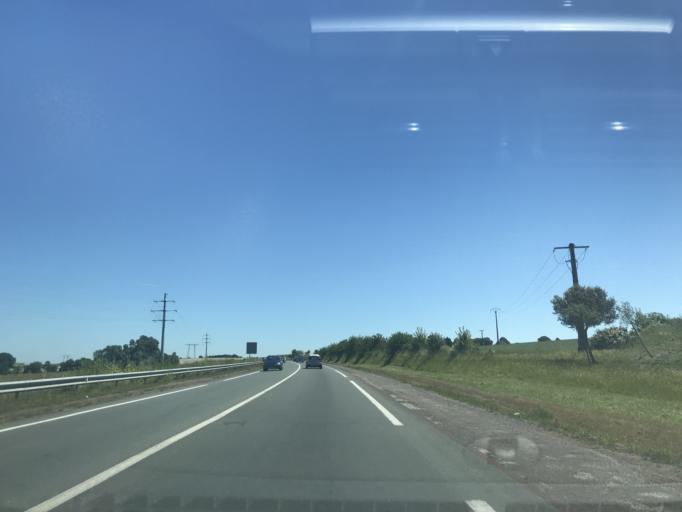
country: FR
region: Poitou-Charentes
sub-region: Departement de la Charente-Maritime
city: Saint-Georges-de-Didonne
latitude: 45.6153
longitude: -0.9868
